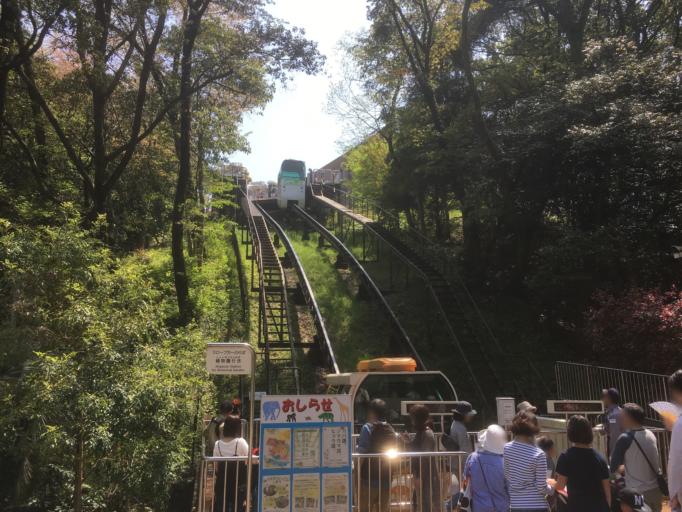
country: JP
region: Fukuoka
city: Fukuoka-shi
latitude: 33.5719
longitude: 130.3885
